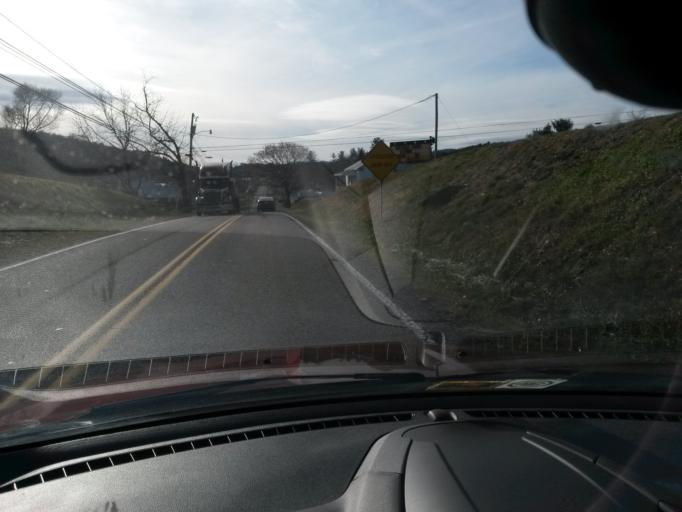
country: US
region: Virginia
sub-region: Rockbridge County
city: East Lexington
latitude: 38.0807
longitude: -79.3795
